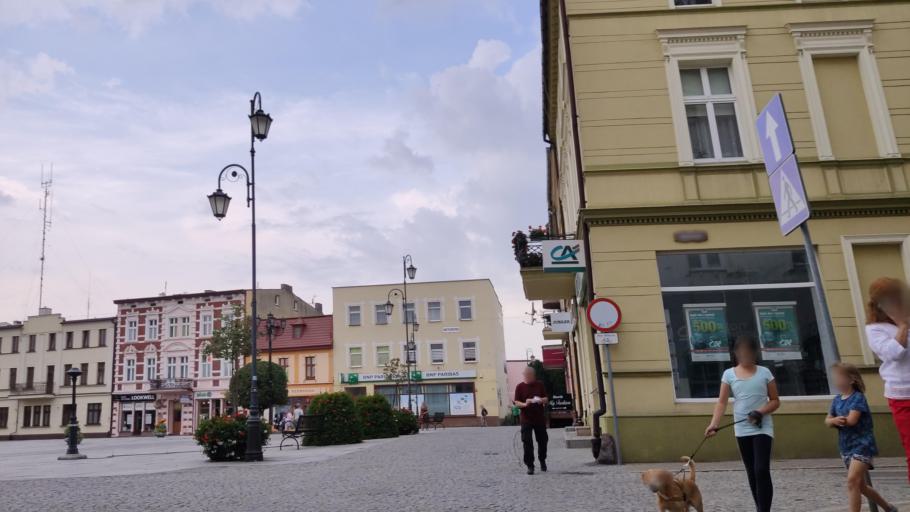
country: PL
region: Kujawsko-Pomorskie
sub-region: Powiat zninski
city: Znin
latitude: 52.8471
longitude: 17.7244
